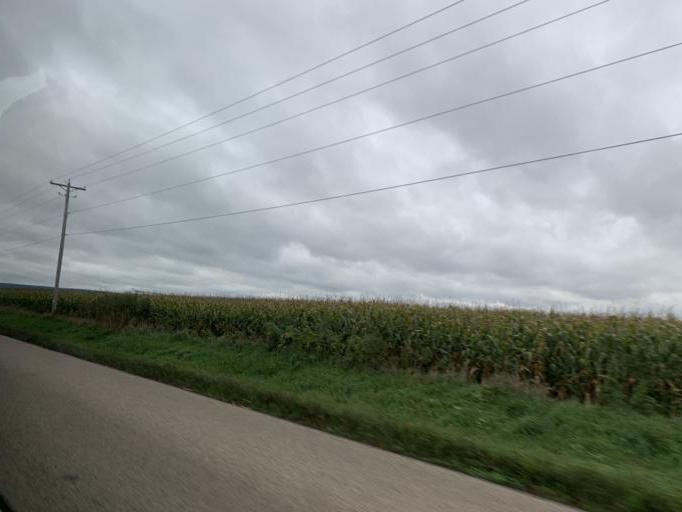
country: US
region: Wisconsin
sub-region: Sauk County
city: Prairie du Sac
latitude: 43.3319
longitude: -89.7703
